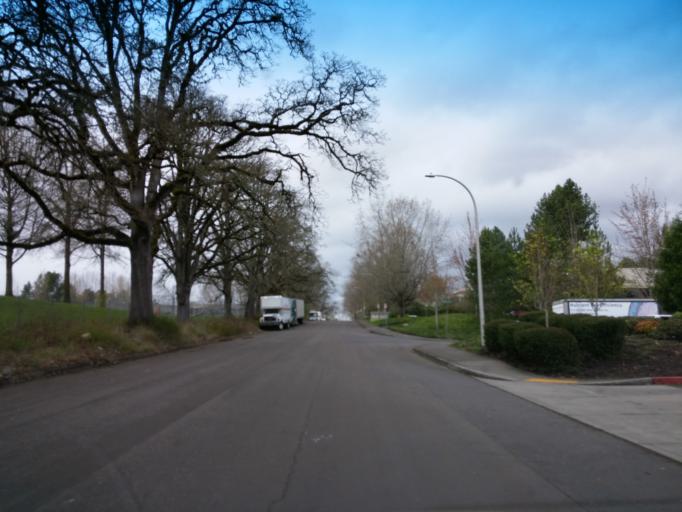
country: US
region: Oregon
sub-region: Washington County
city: Oak Hills
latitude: 45.5297
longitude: -122.8490
